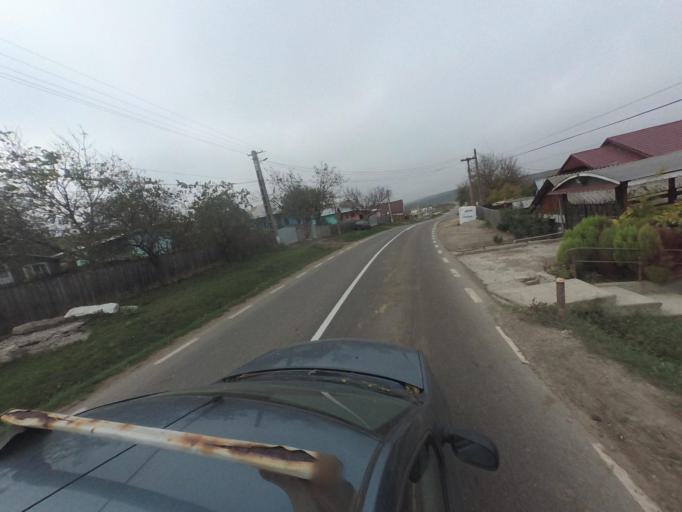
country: RO
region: Vaslui
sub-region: Comuna Bacesti
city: Bacesti
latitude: 46.8351
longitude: 27.2300
